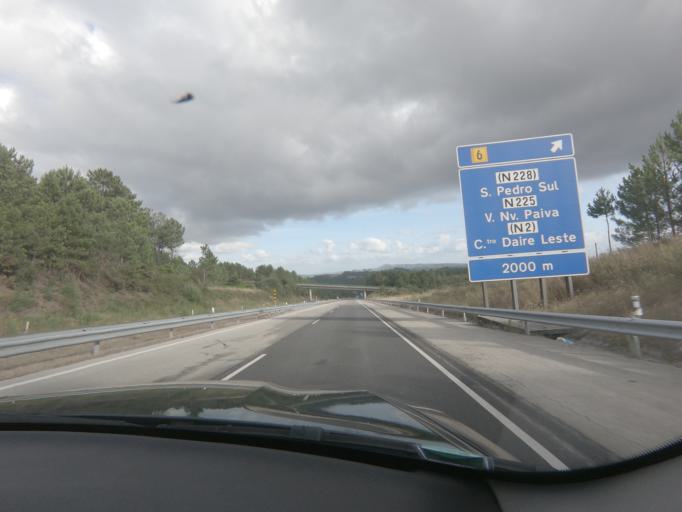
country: PT
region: Viseu
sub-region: Castro Daire
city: Castro Daire
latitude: 40.9174
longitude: -7.9138
